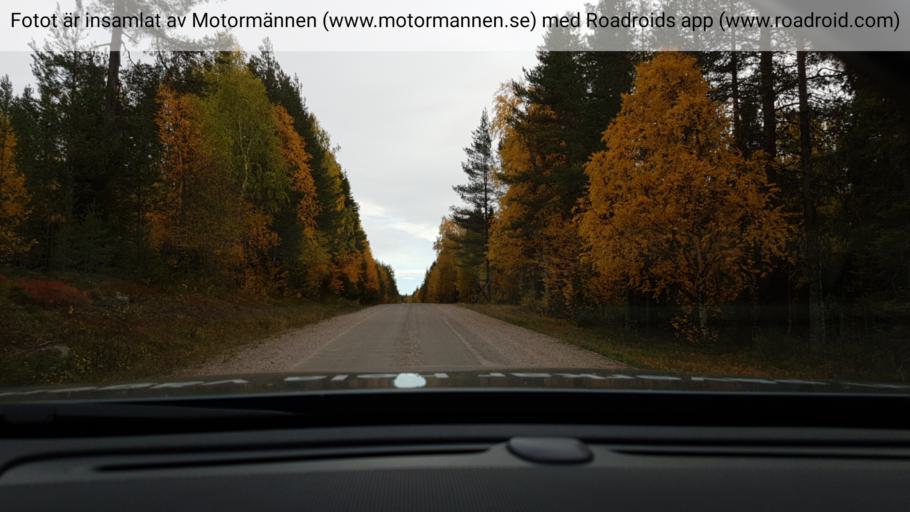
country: SE
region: Norrbotten
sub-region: Overkalix Kommun
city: OEverkalix
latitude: 66.2719
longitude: 22.9939
